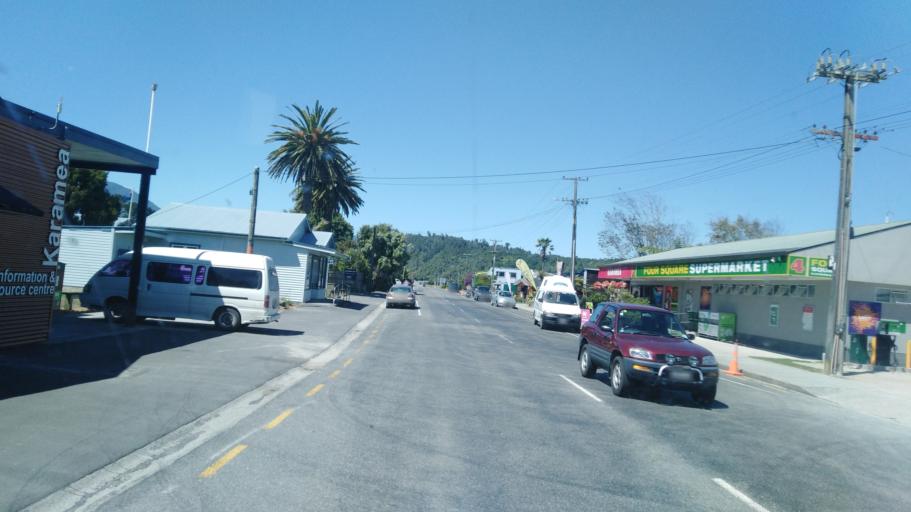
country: NZ
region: West Coast
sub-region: Buller District
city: Westport
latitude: -41.2512
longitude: 172.1285
